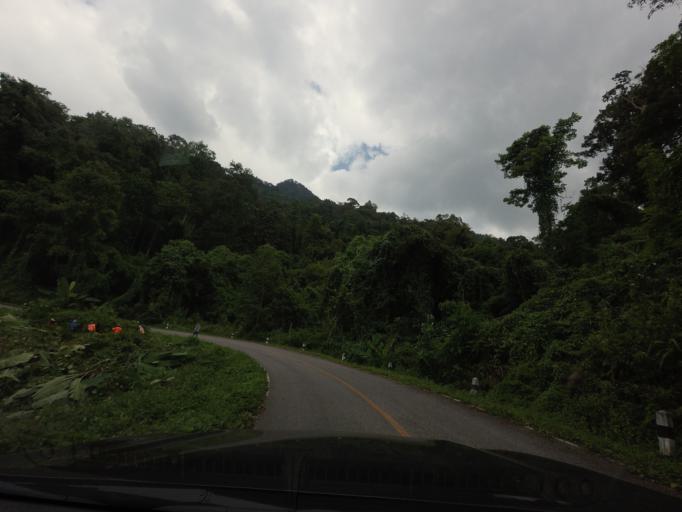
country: TH
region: Uttaradit
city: Nam Pat
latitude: 17.7237
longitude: 100.9474
